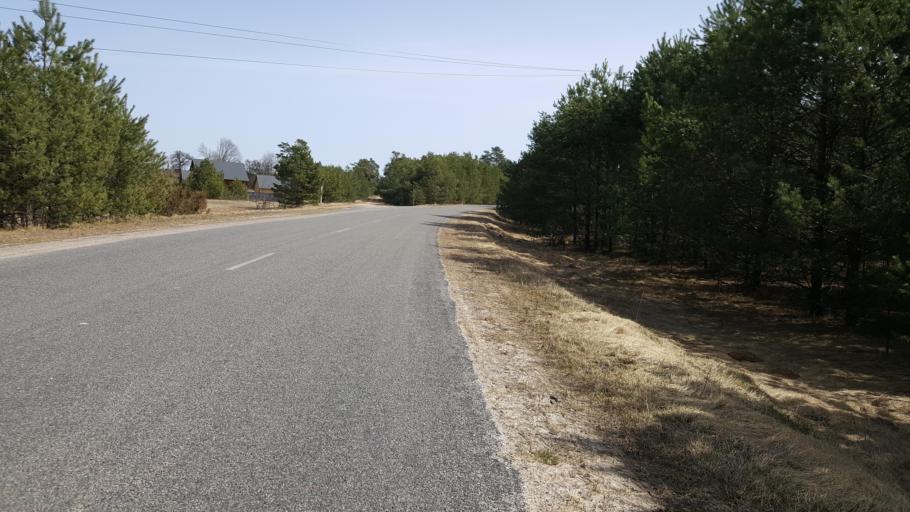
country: BY
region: Brest
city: Kamyanyuki
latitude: 52.5286
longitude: 23.8375
